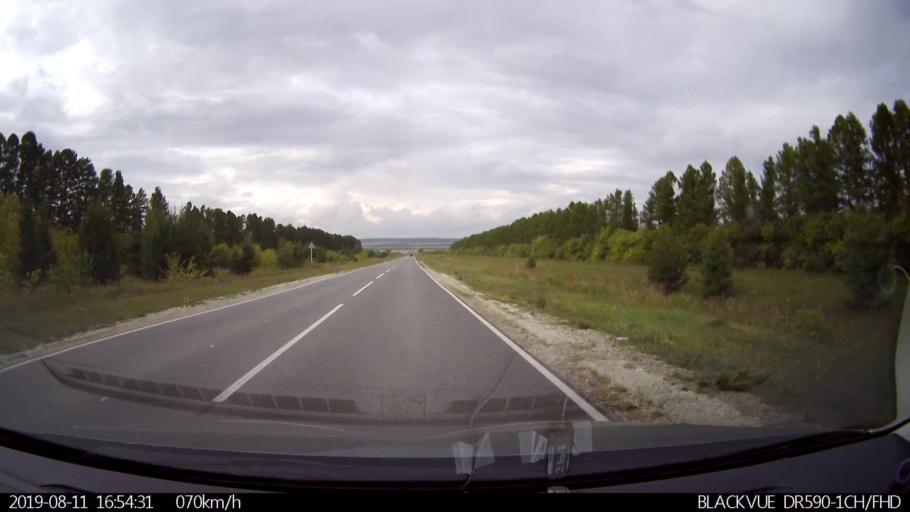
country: RU
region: Ulyanovsk
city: Mayna
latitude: 54.2735
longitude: 47.6662
